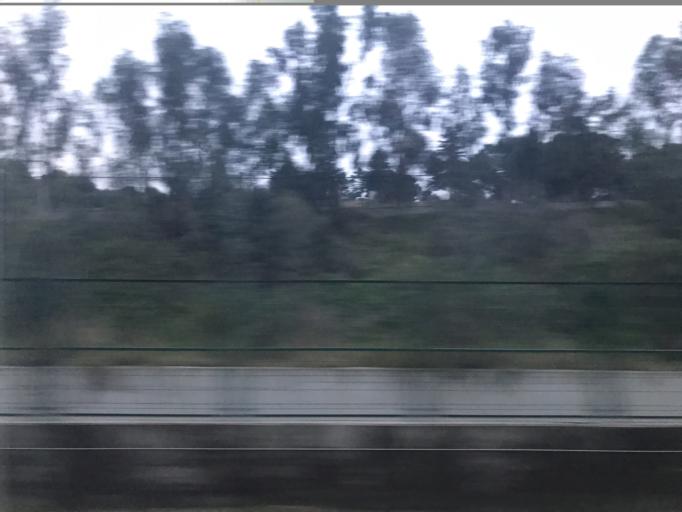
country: TR
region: Kocaeli
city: Darica
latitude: 40.8062
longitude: 29.3688
